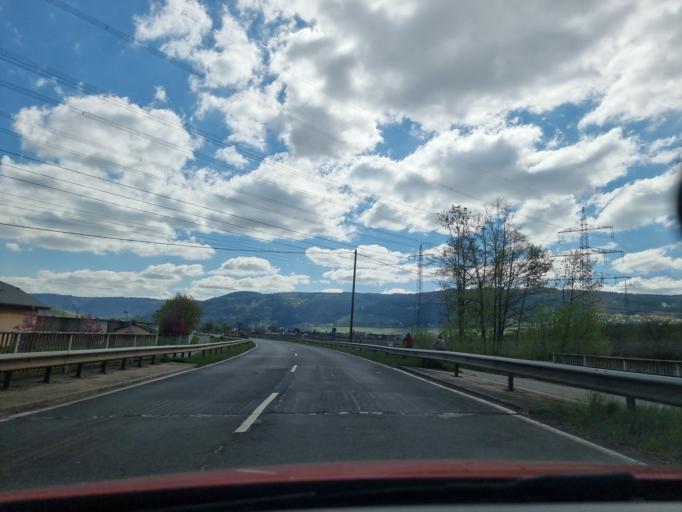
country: DE
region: Rheinland-Pfalz
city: Longuich
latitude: 49.8005
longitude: 6.7813
